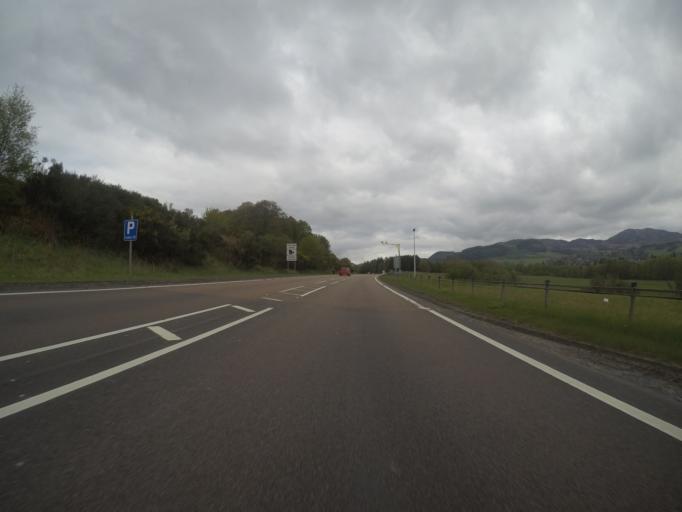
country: GB
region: Scotland
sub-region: Perth and Kinross
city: Pitlochry
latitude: 56.6929
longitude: -3.7272
